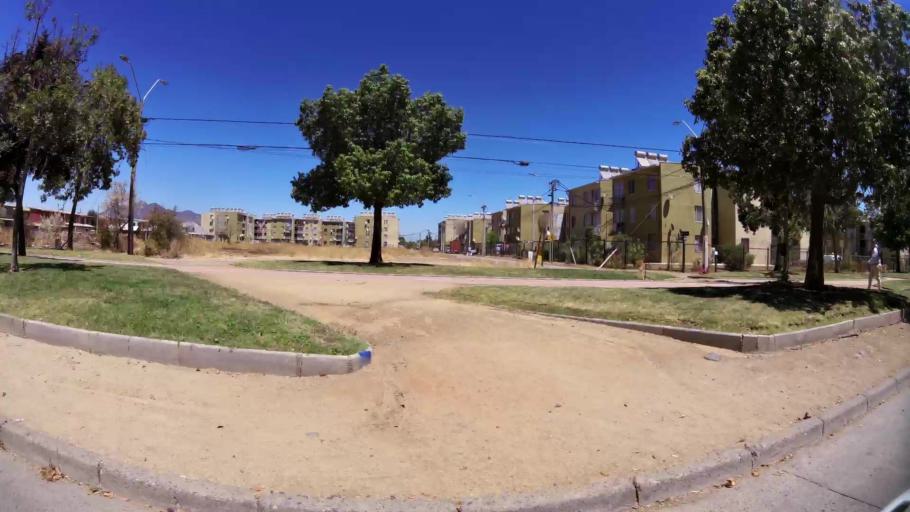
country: CL
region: O'Higgins
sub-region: Provincia de Cachapoal
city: Rancagua
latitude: -34.1629
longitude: -70.7026
